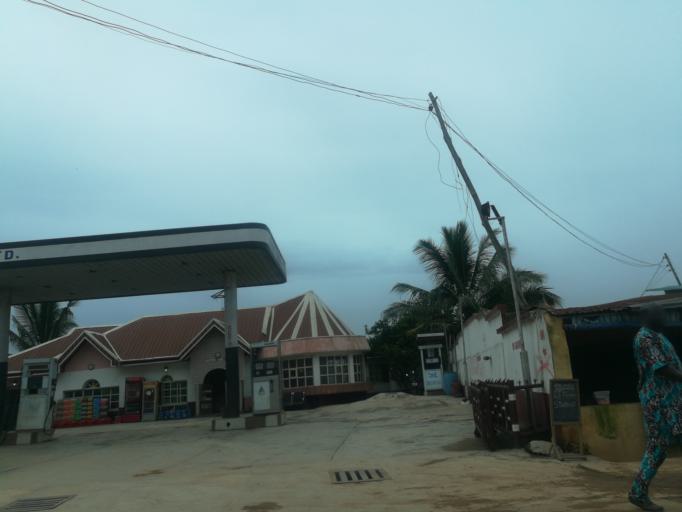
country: NG
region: Oyo
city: Ibadan
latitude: 7.3341
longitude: 3.8922
